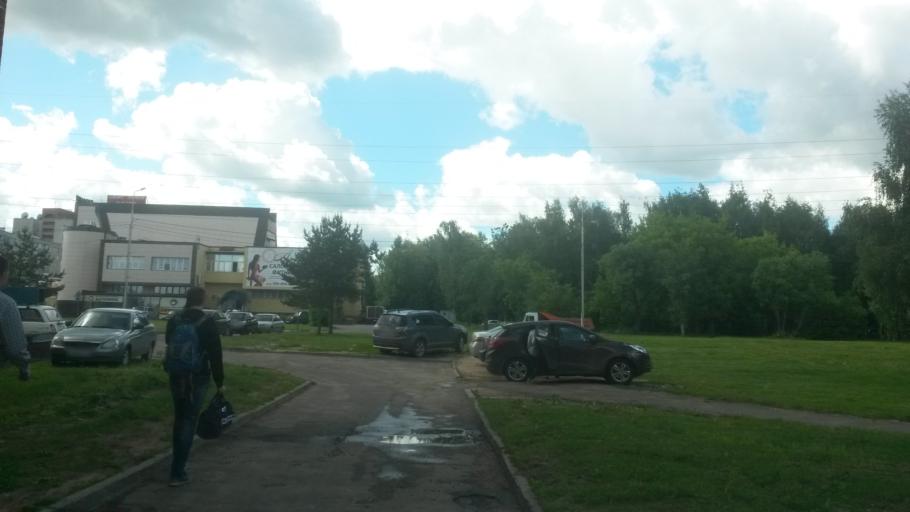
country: RU
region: Jaroslavl
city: Yaroslavl
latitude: 57.5865
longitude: 39.8547
